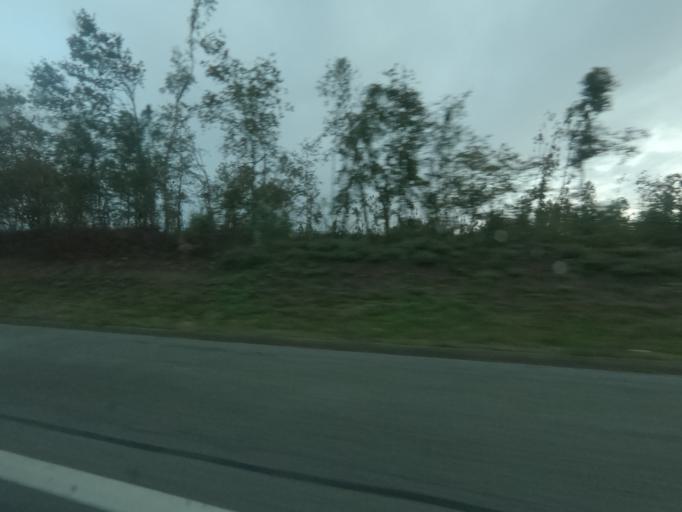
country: PT
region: Braga
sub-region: Vila Verde
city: Prado
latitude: 41.5453
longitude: -8.5011
